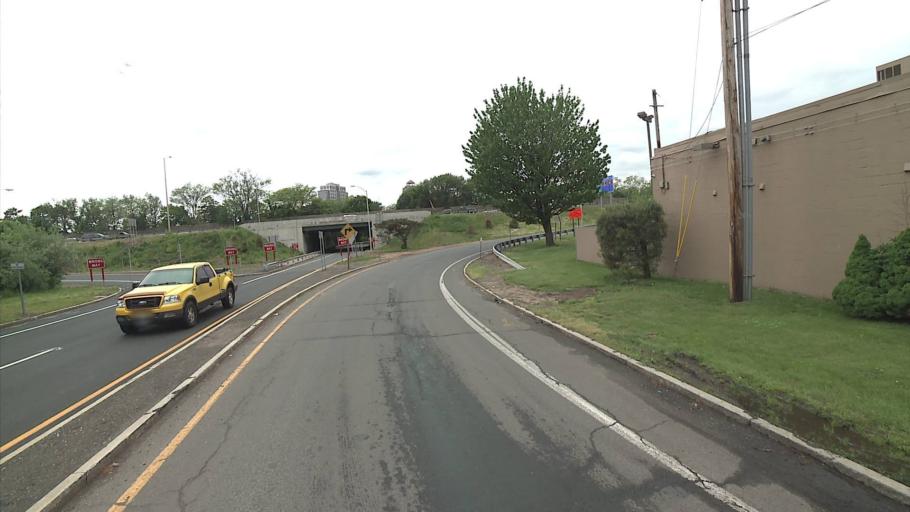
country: US
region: Connecticut
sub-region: New Haven County
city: New Haven
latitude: 41.3056
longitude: -72.9129
